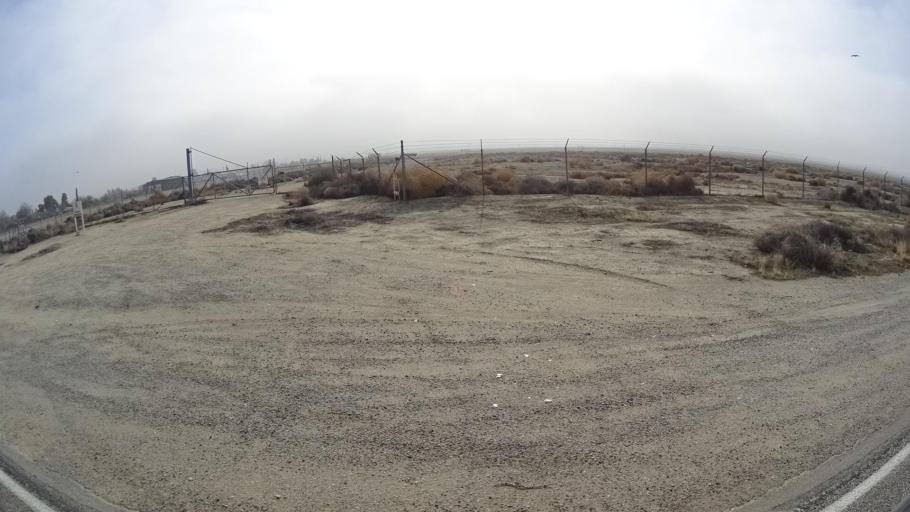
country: US
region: California
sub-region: Kern County
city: Ford City
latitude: 35.2097
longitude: -119.4135
